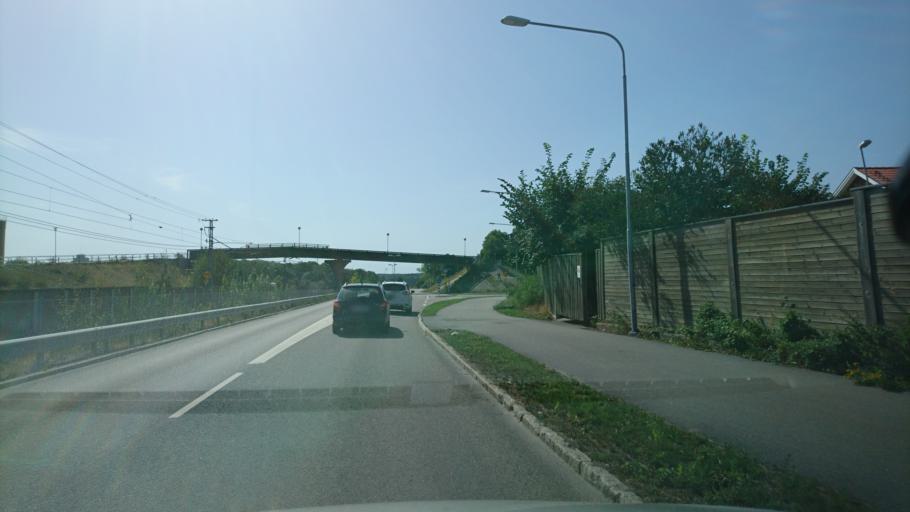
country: SE
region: Soedermanland
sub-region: Strangnas Kommun
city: Strangnas
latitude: 59.3648
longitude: 17.0377
